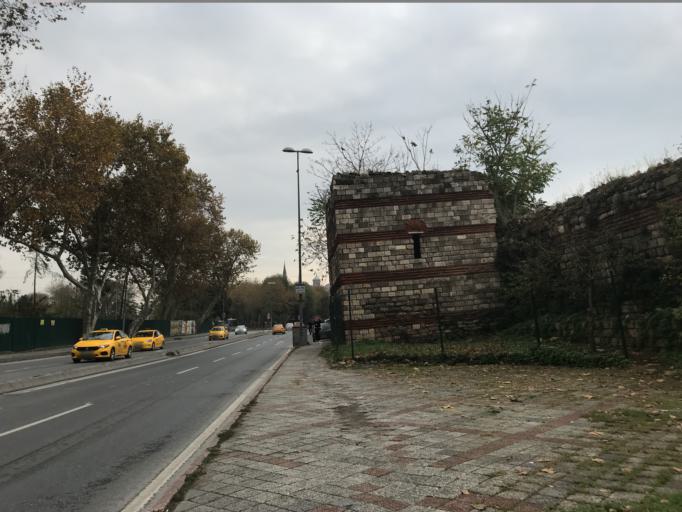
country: TR
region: Istanbul
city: Istanbul
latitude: 41.0364
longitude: 28.9457
